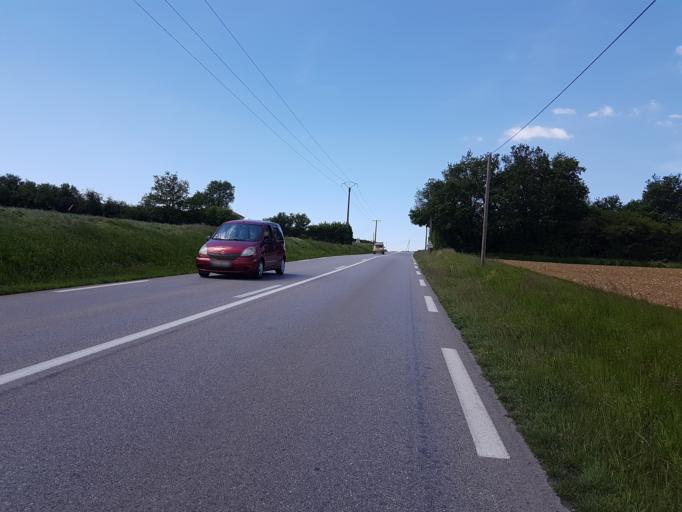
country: FR
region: Rhone-Alpes
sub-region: Departement de l'Isere
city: Chavanoz
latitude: 45.7835
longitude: 5.1581
